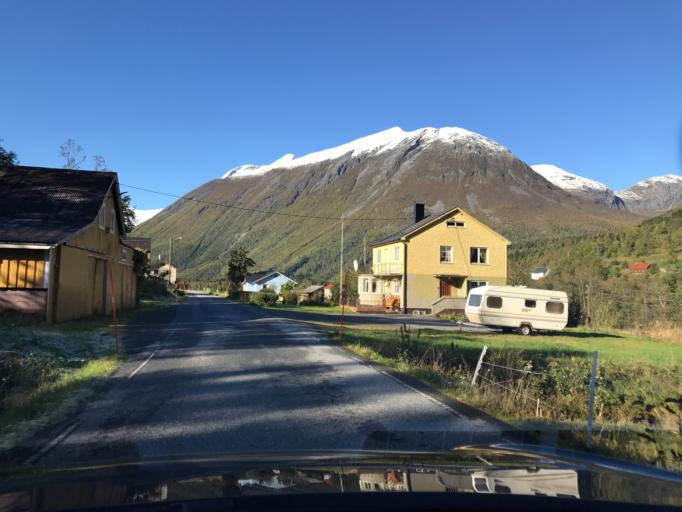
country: NO
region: More og Romsdal
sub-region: Norddal
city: Valldal
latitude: 62.3304
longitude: 7.3817
